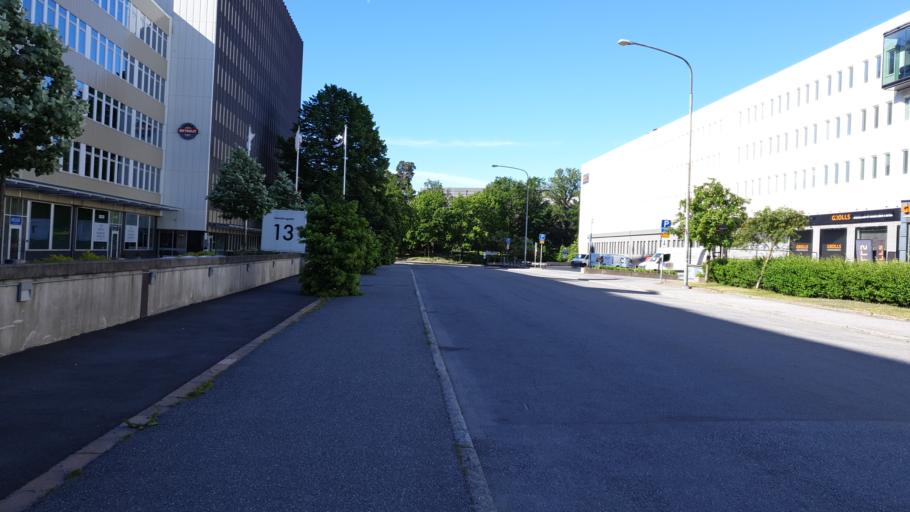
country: SE
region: Stockholm
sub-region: Sundbybergs Kommun
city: Sundbyberg
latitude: 59.3539
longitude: 17.9758
